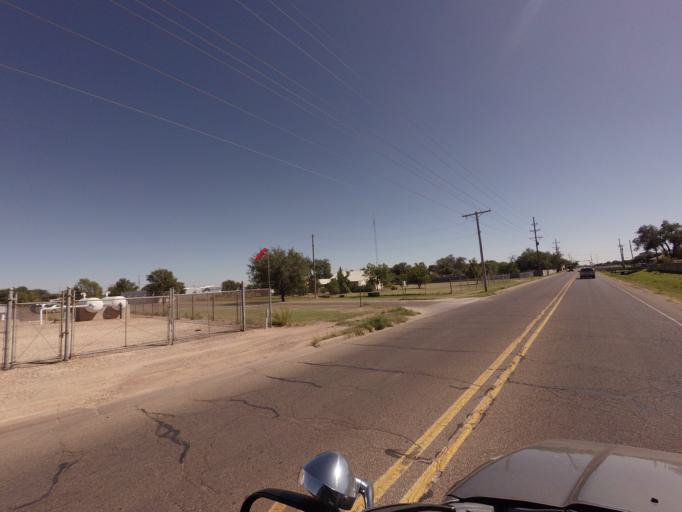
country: US
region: New Mexico
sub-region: Curry County
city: Clovis
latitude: 34.4068
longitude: -103.2317
